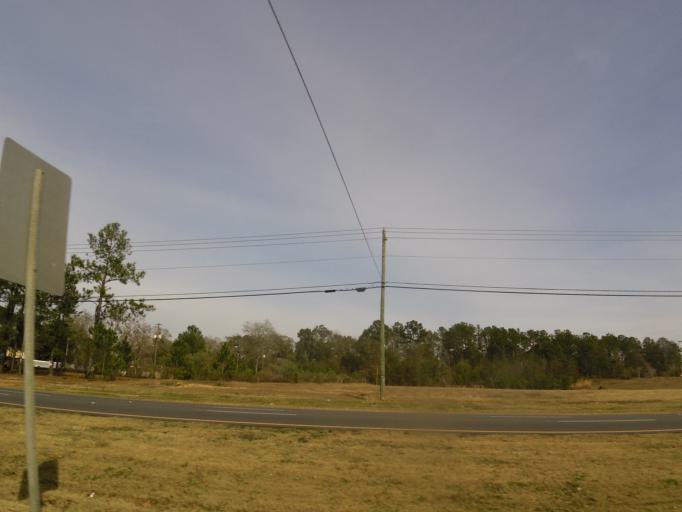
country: US
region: Alabama
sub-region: Houston County
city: Dothan
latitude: 31.2615
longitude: -85.4382
